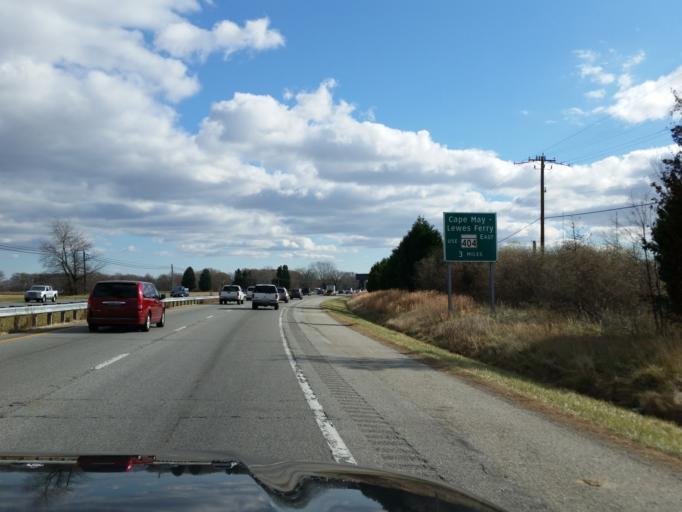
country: US
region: Maryland
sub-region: Queen Anne's County
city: Centreville
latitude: 38.9640
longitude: -76.1041
